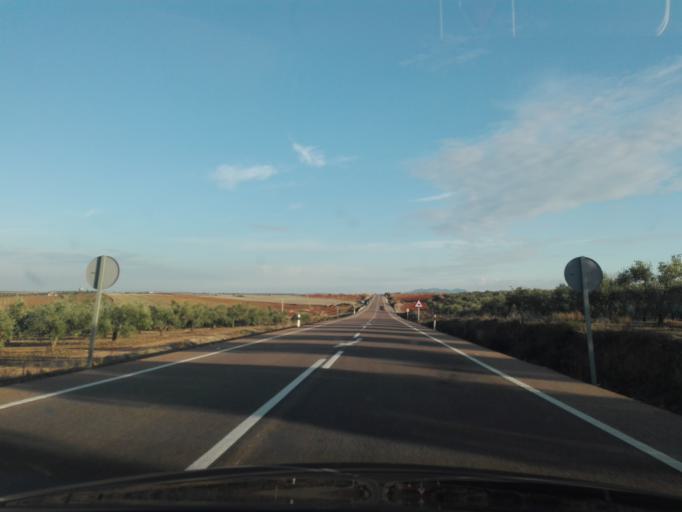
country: ES
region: Extremadura
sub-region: Provincia de Badajoz
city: Usagre
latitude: 38.3405
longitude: -6.1633
